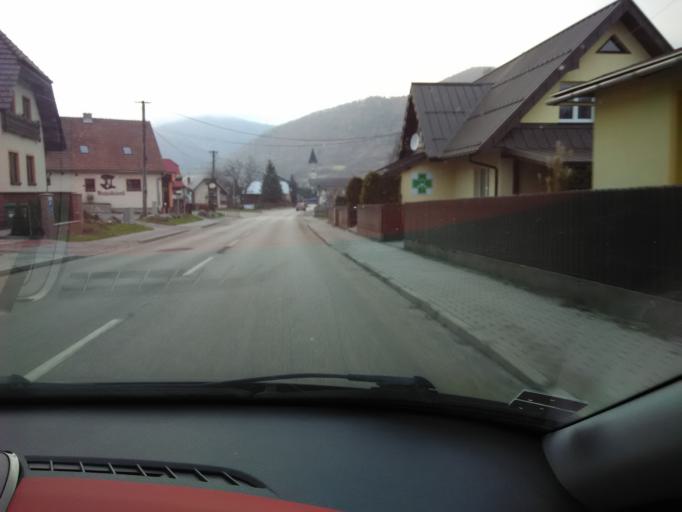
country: SK
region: Zilinsky
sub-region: Okres Zilina
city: Terchova
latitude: 49.2568
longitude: 19.0374
